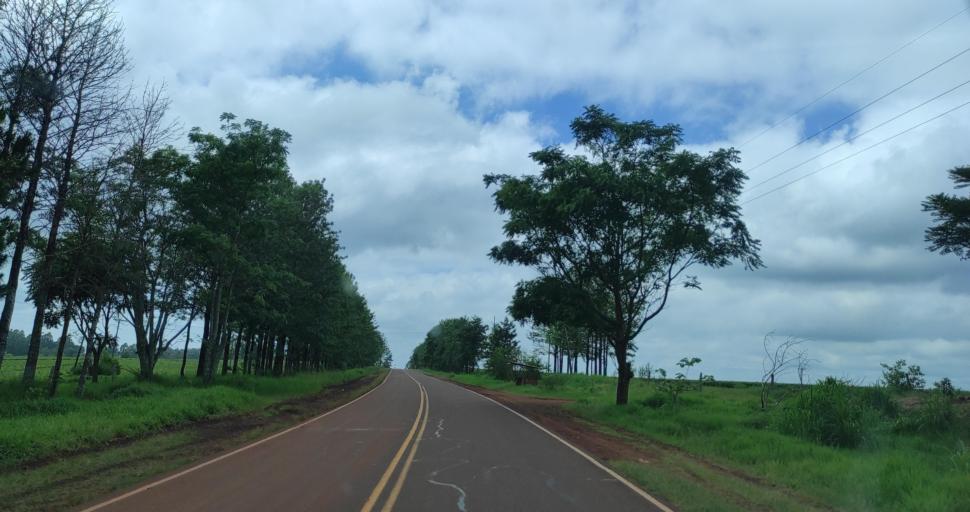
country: AR
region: Misiones
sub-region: Departamento de Veinticinco de Mayo
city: Veinticinco de Mayo
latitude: -27.4053
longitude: -54.7495
